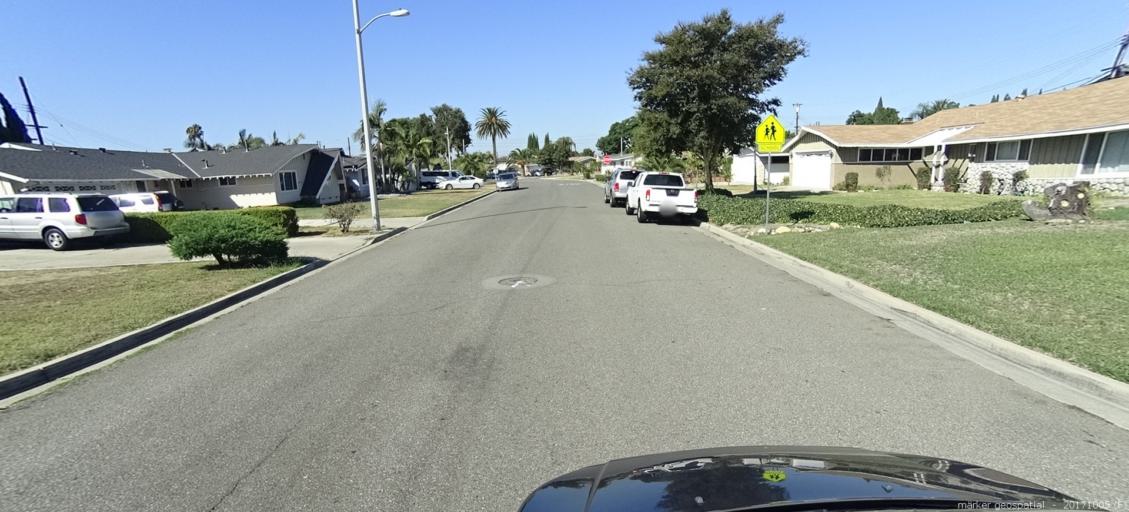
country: US
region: California
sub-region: Orange County
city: Stanton
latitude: 33.8009
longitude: -117.9766
